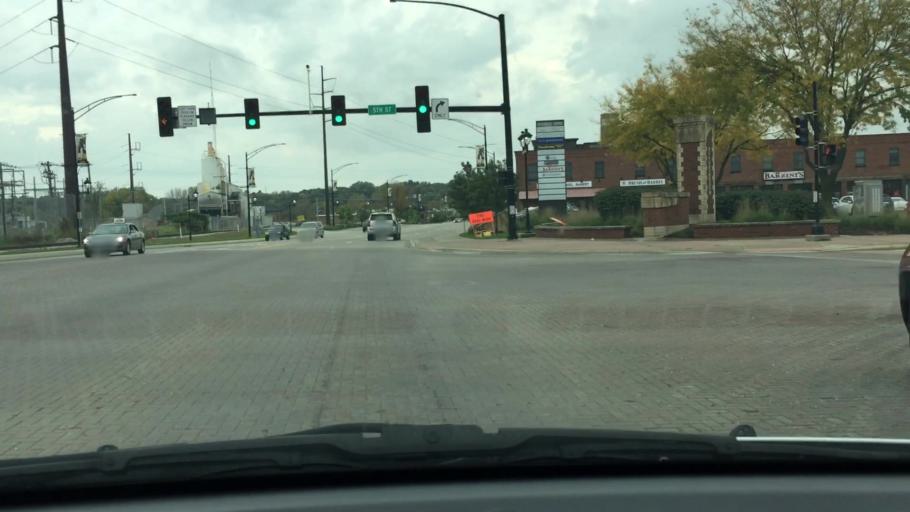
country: US
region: Iowa
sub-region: Johnson County
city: Coralville
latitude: 41.6737
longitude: -91.5658
